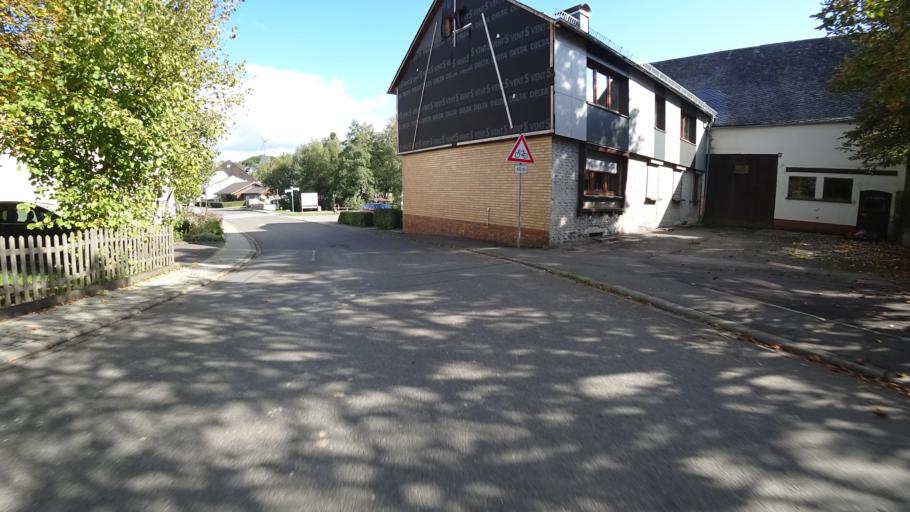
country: DE
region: Rheinland-Pfalz
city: Neuerkirch
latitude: 50.0129
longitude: 7.4889
